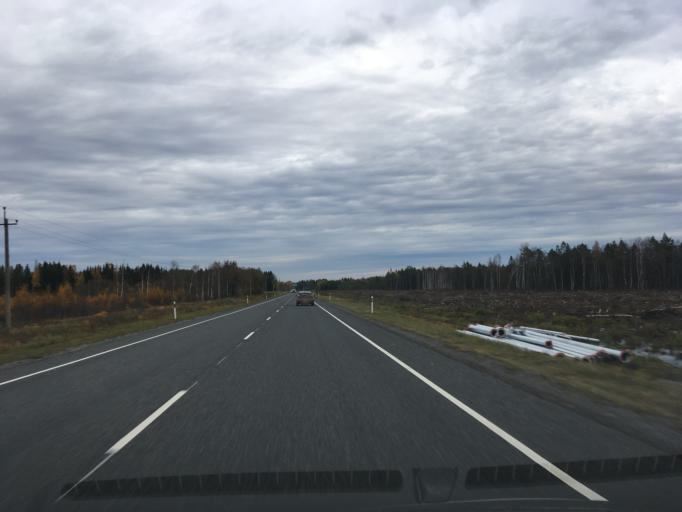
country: EE
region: Harju
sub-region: Nissi vald
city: Turba
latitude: 58.9851
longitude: 24.0578
